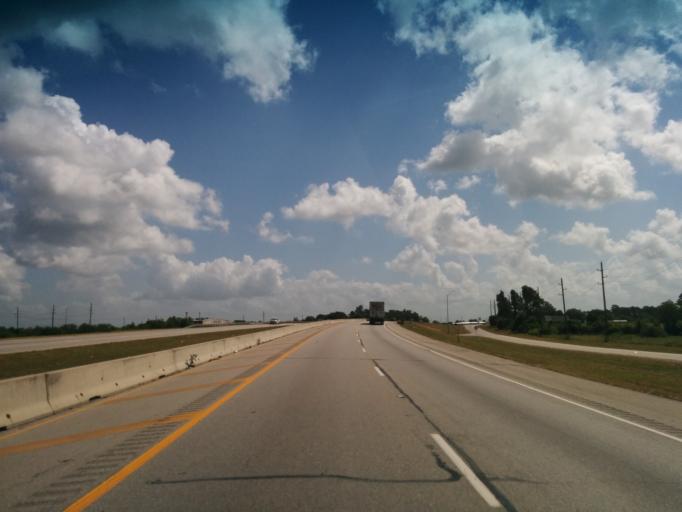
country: US
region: Texas
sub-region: Austin County
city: Sealy
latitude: 29.7719
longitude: -96.1359
